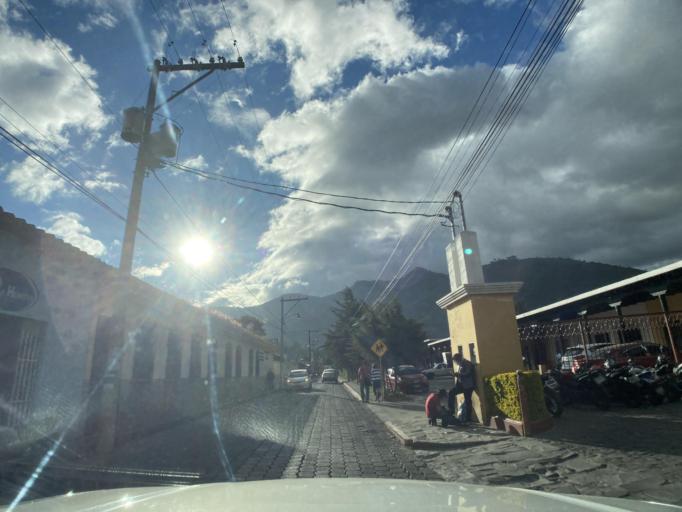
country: GT
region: Sacatepequez
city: Jocotenango
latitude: 14.5746
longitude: -90.7429
